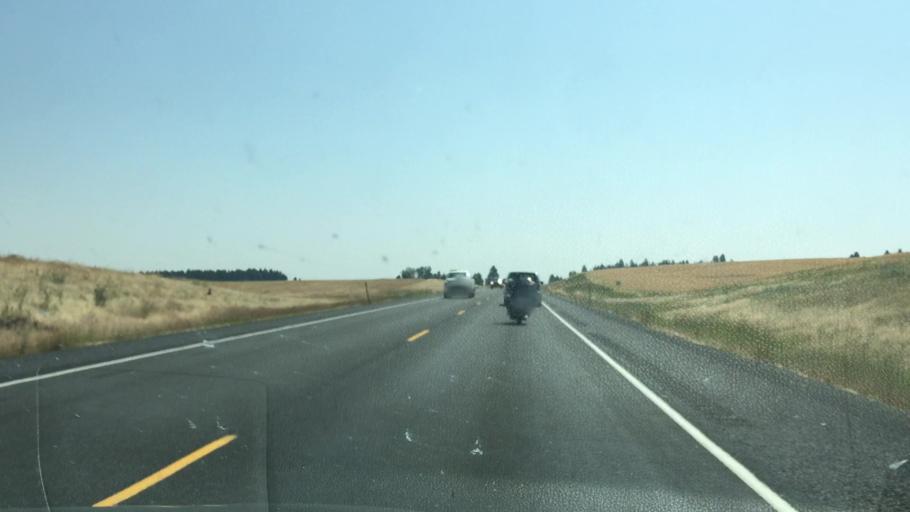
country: US
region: Idaho
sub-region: Nez Perce County
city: Lapwai
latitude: 46.2449
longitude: -116.5894
